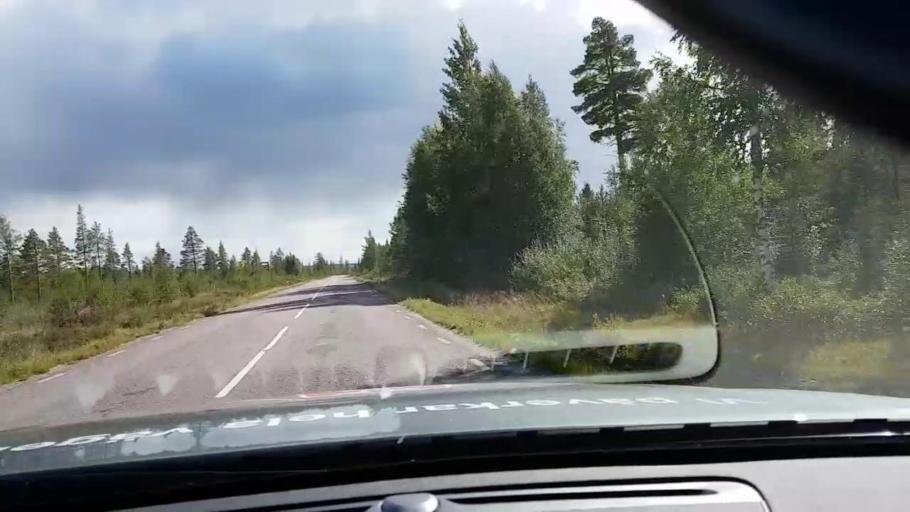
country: SE
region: Vaesterbotten
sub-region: Asele Kommun
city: Asele
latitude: 63.8998
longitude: 17.3485
